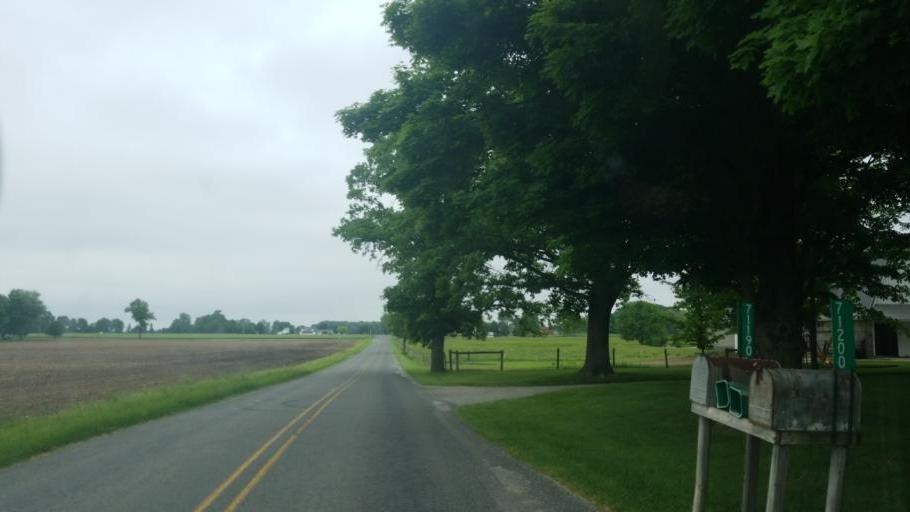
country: US
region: Indiana
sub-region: Elkhart County
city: Nappanee
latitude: 41.4616
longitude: -86.0497
